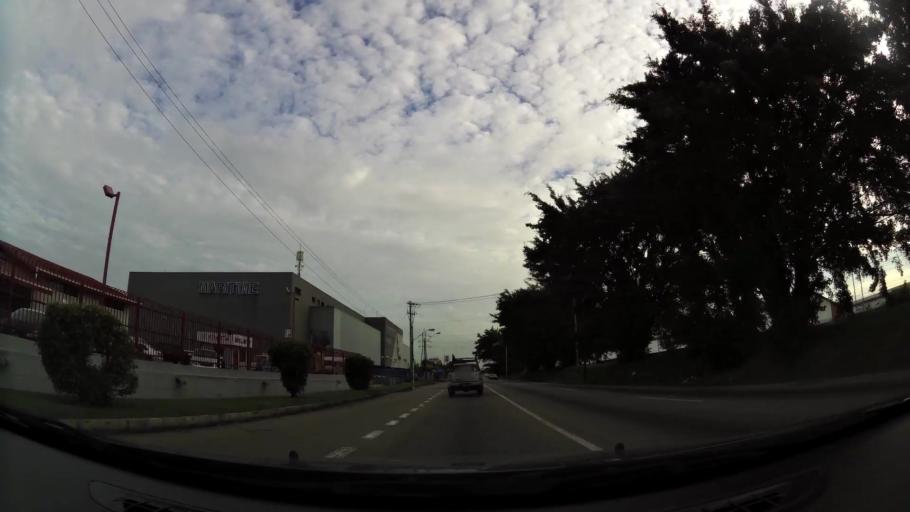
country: TT
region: San Juan/Laventille
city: Laventille
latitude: 10.6472
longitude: -61.4696
